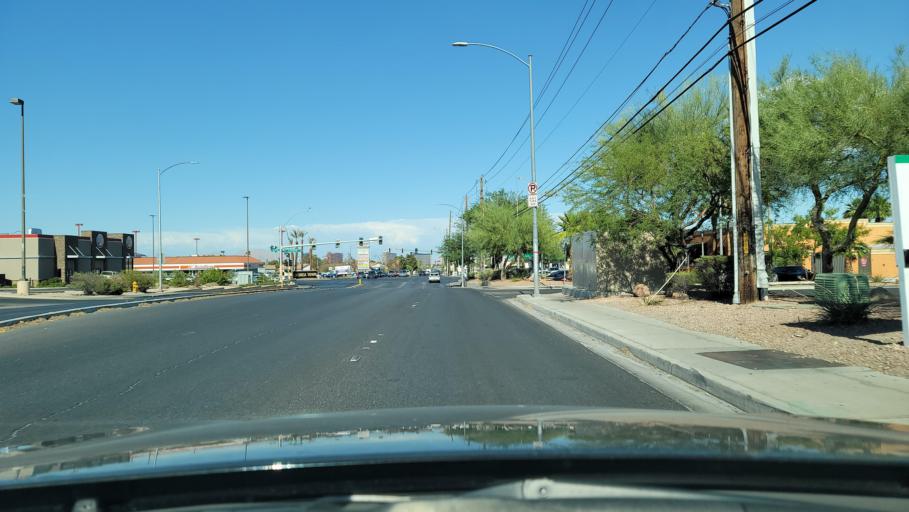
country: US
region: Nevada
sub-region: Clark County
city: Spring Valley
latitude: 36.1257
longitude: -115.2445
